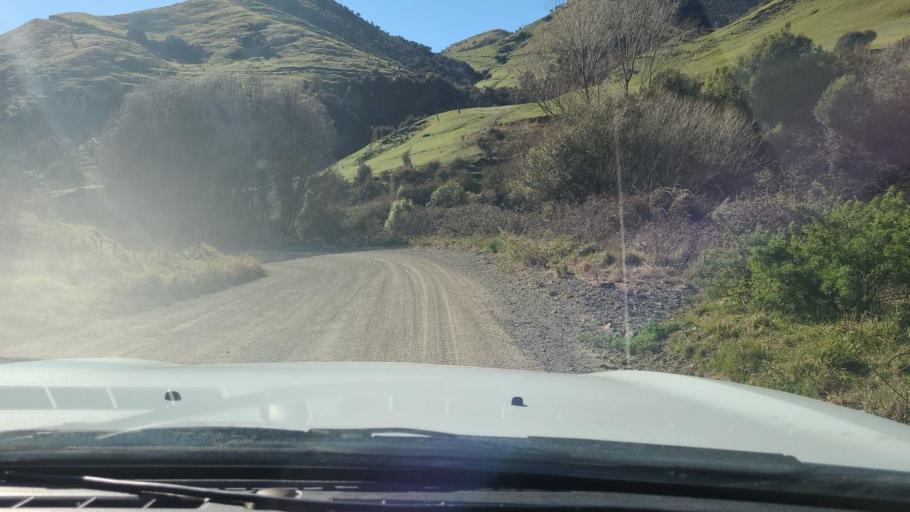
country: NZ
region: Hawke's Bay
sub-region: Napier City
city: Taradale
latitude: -39.2262
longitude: 176.5025
